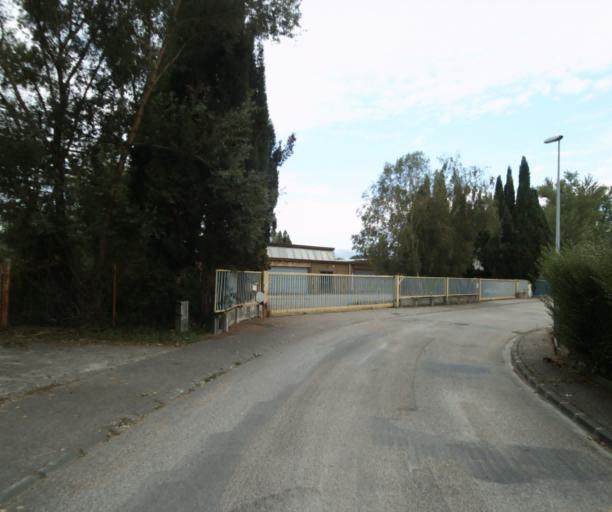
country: FR
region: Rhone-Alpes
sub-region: Departement de l'Isere
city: Domene
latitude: 45.1988
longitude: 5.8232
